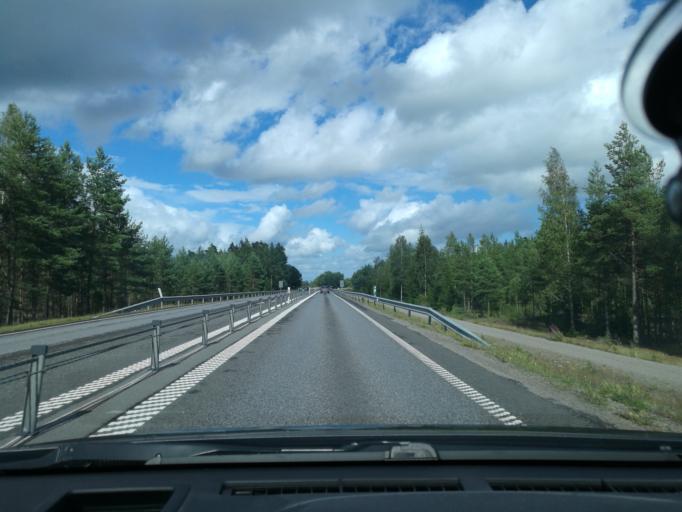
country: SE
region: Kronoberg
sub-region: Alvesta Kommun
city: Vislanda
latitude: 56.7241
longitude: 14.4658
